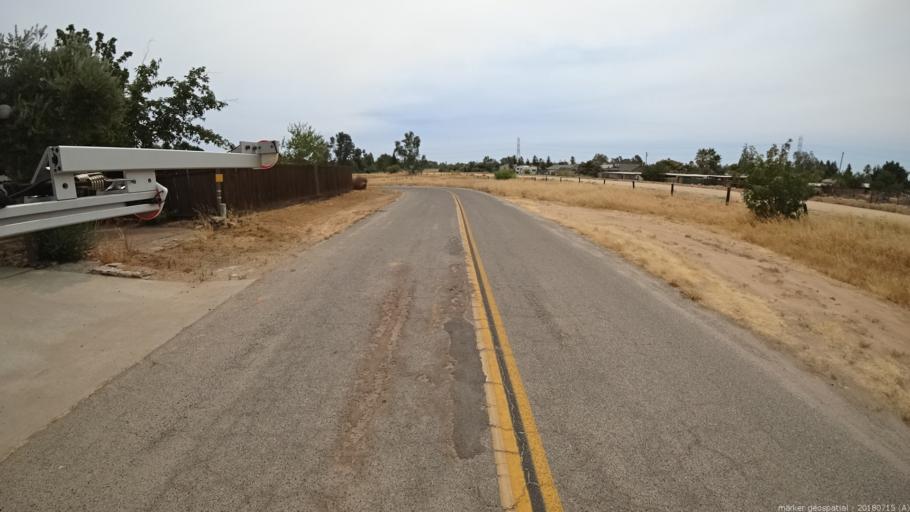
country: US
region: California
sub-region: Madera County
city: Madera Acres
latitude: 37.0213
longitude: -120.0822
